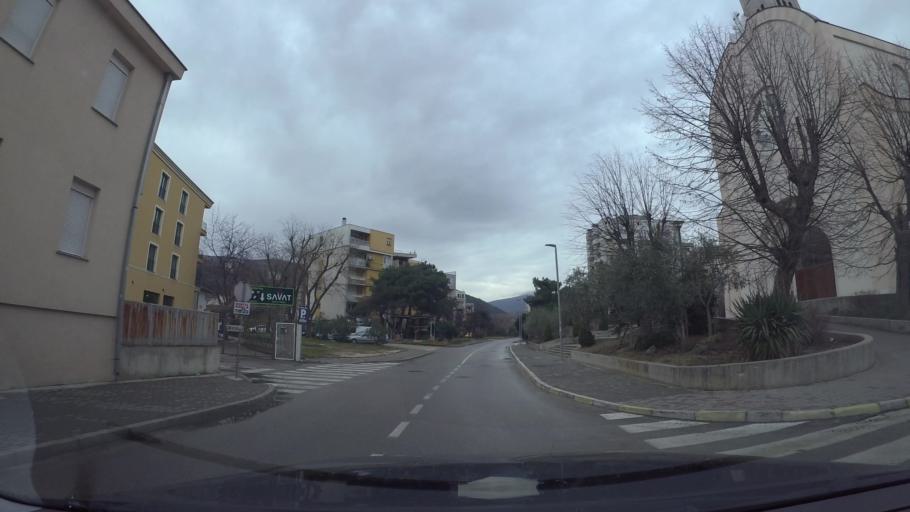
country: BA
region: Federation of Bosnia and Herzegovina
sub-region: Hercegovacko-Bosanski Kanton
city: Mostar
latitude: 43.3374
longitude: 17.8093
